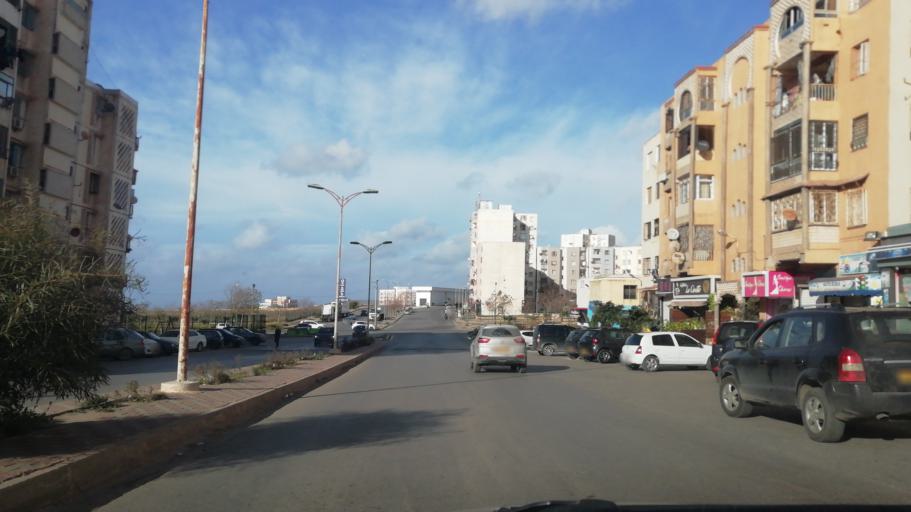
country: DZ
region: Oran
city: Bir el Djir
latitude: 35.7191
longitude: -0.5960
